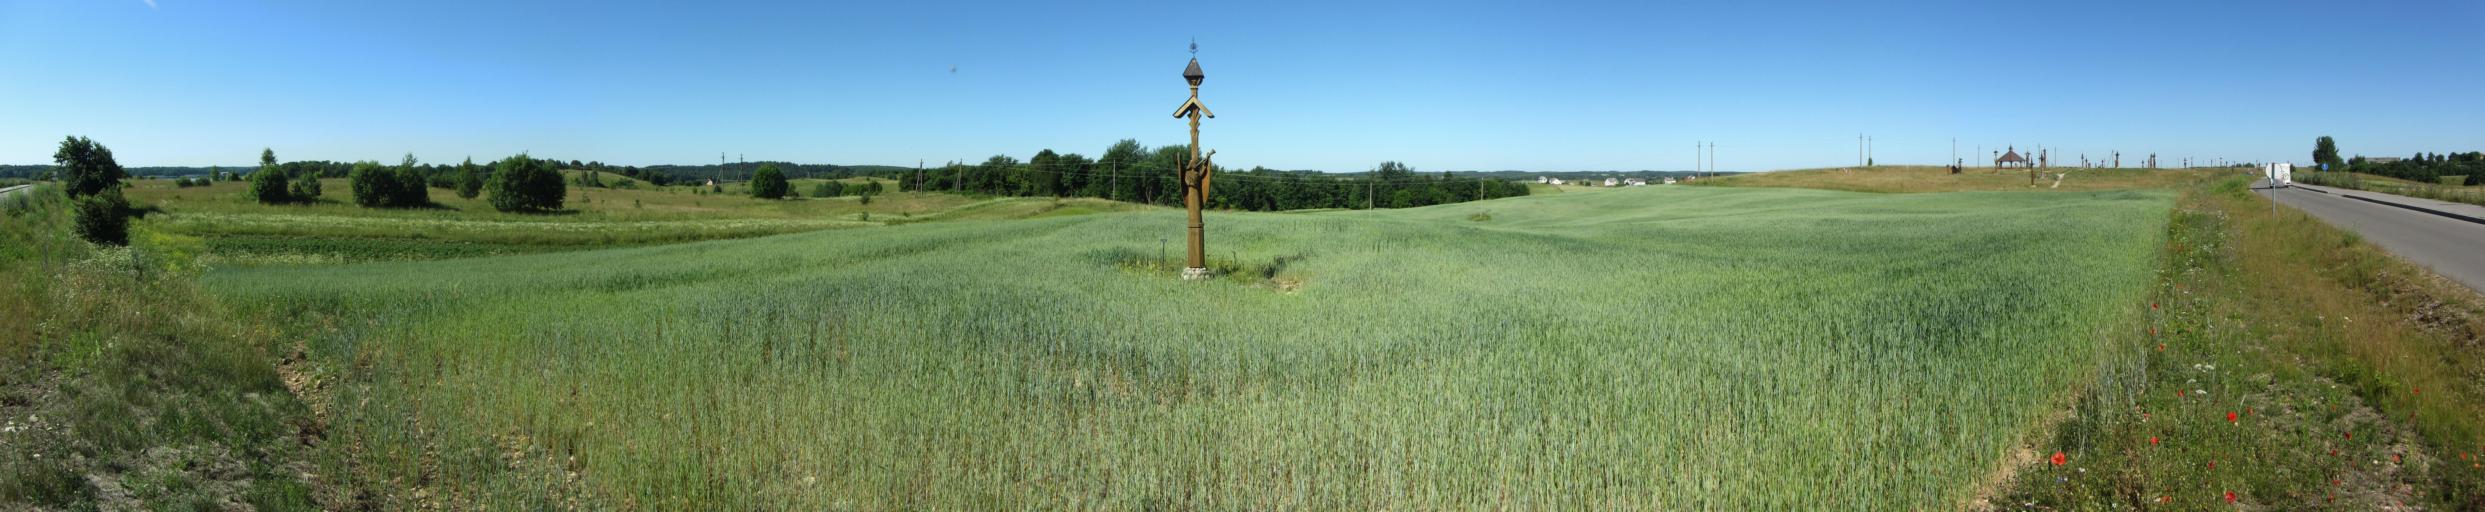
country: LT
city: Trakai
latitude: 54.6751
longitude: 24.9295
